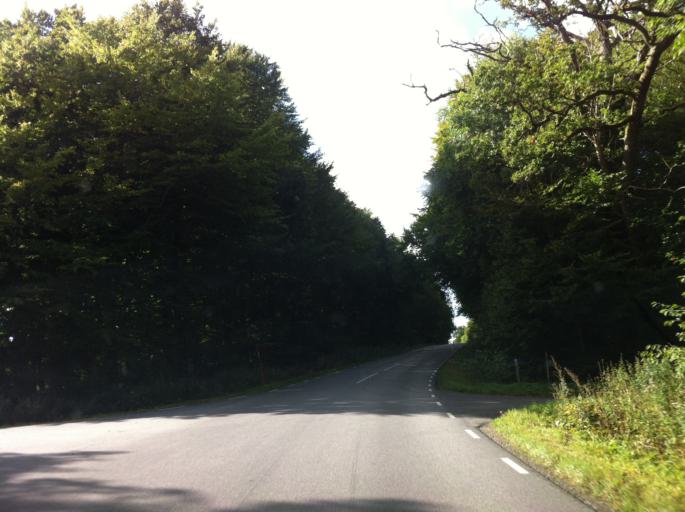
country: SE
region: Skane
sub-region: Tomelilla Kommun
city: Tomelilla
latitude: 55.6528
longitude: 13.9424
